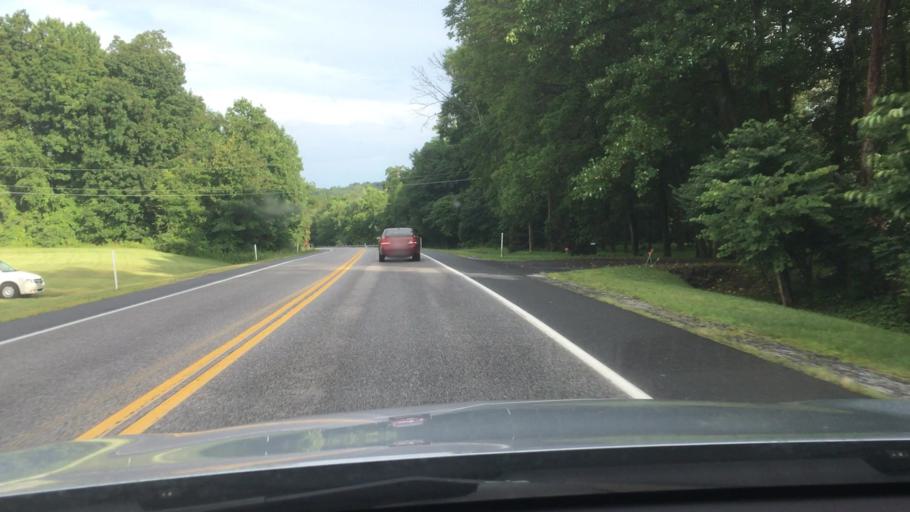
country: US
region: Pennsylvania
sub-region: York County
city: Dillsburg
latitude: 40.0841
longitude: -76.9416
